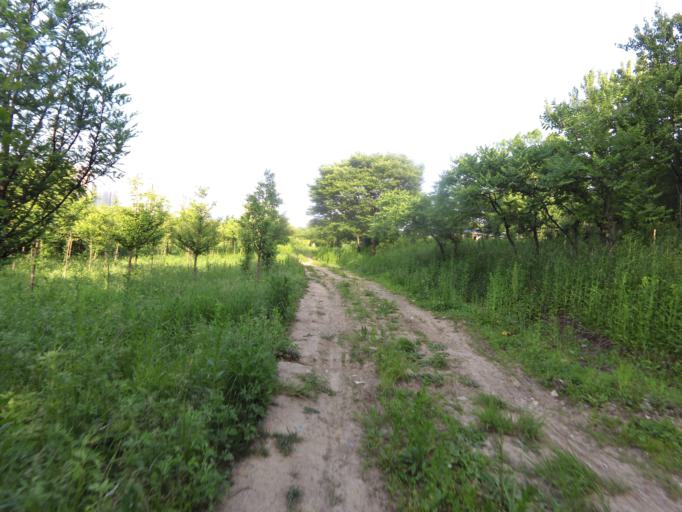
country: KR
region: Gyeongsangbuk-do
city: Gyeongsan-si
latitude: 35.8375
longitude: 128.7618
